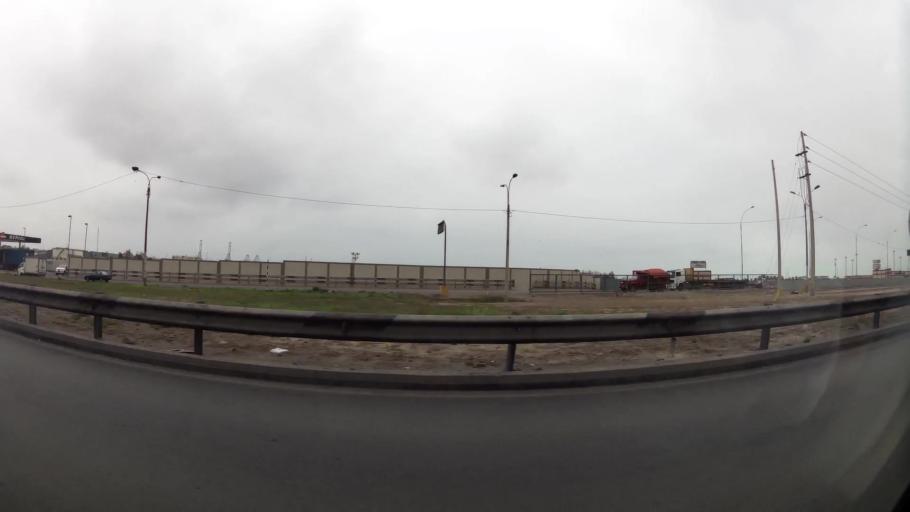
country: PE
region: Callao
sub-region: Callao
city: Callao
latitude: -12.0372
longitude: -77.1268
